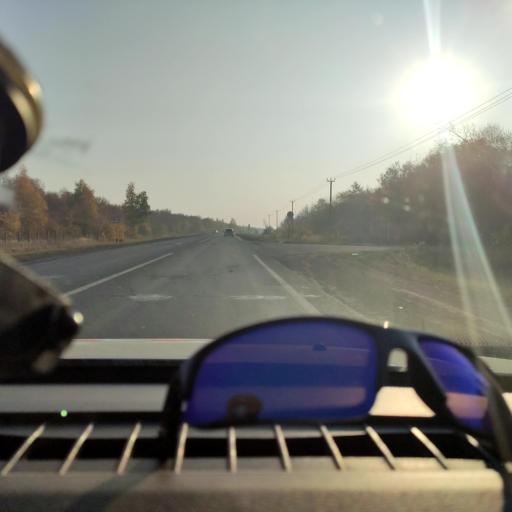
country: RU
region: Samara
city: Chapayevsk
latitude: 52.9959
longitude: 49.8014
